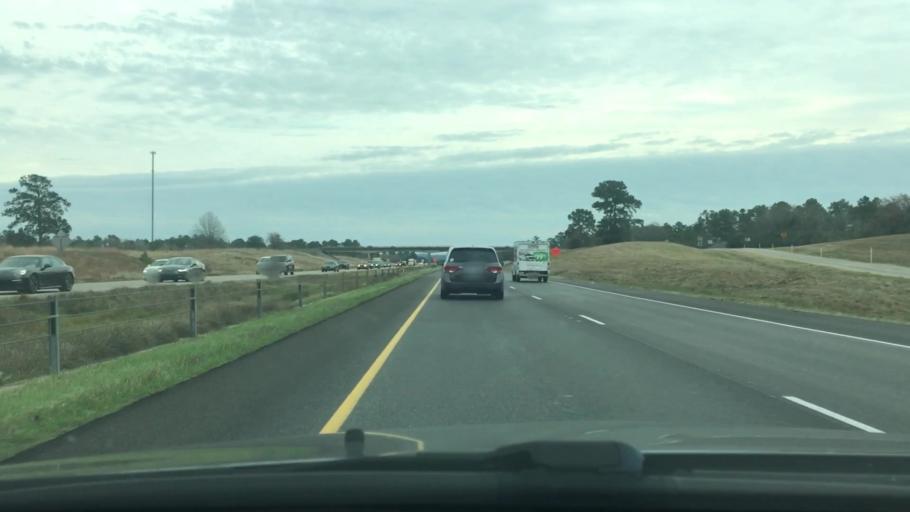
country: US
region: Texas
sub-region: Madison County
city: Madisonville
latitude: 30.8756
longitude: -95.7622
